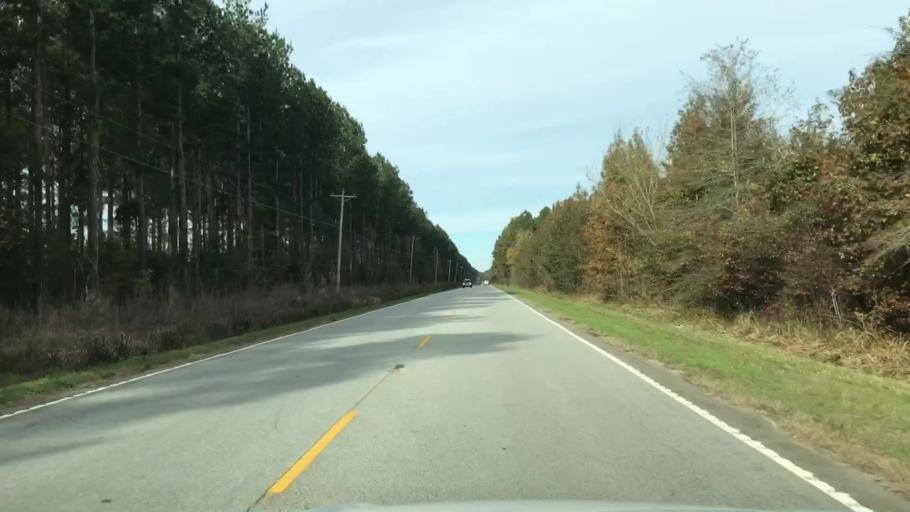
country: US
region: South Carolina
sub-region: Colleton County
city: Walterboro
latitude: 32.8139
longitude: -80.5344
